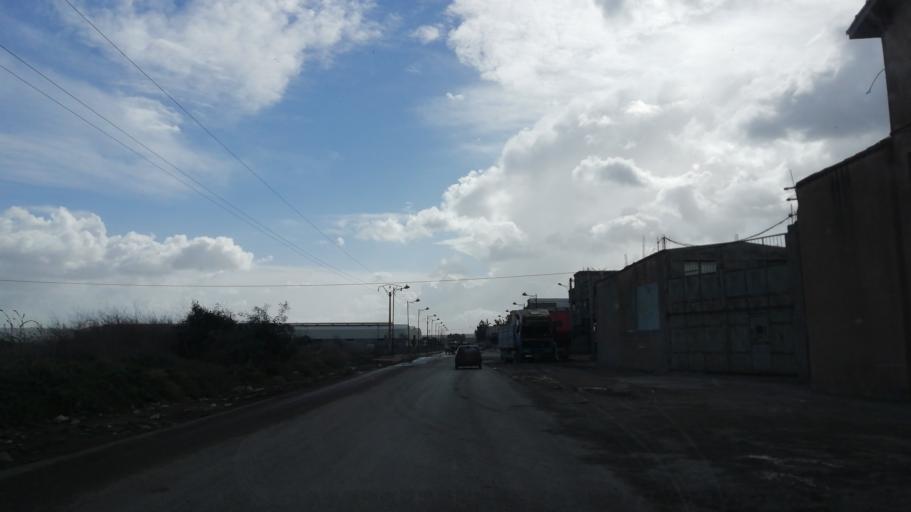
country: DZ
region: Oran
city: Sidi ech Chahmi
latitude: 35.6439
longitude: -0.5565
